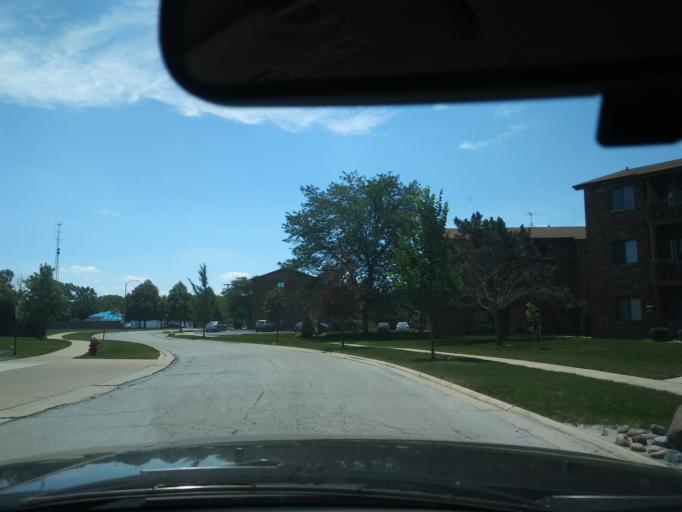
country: US
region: Illinois
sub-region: Cook County
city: Oak Forest
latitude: 41.6047
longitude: -87.7603
